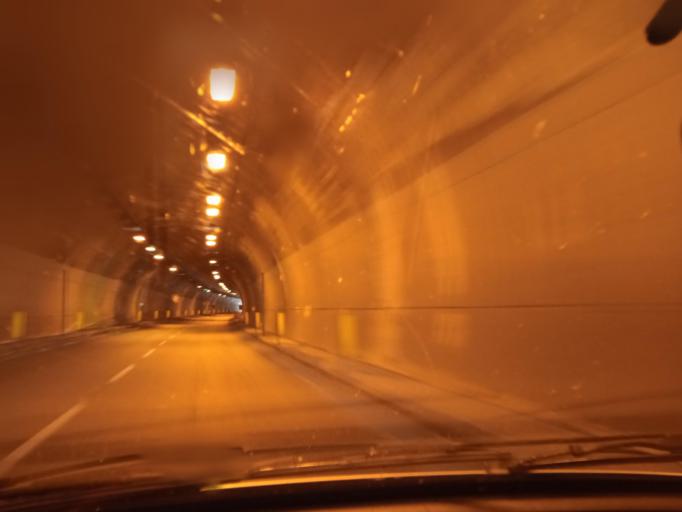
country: IT
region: Sicily
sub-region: Messina
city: Acquedolci
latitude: 38.0543
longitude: 14.6051
